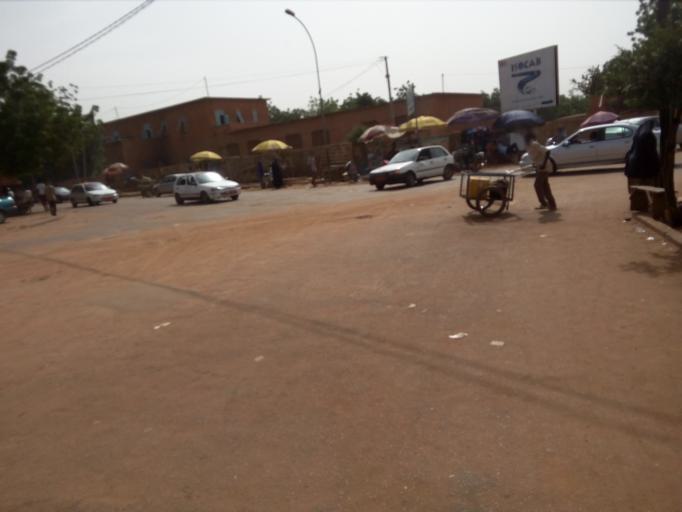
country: NE
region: Niamey
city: Niamey
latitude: 13.5132
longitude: 2.1136
